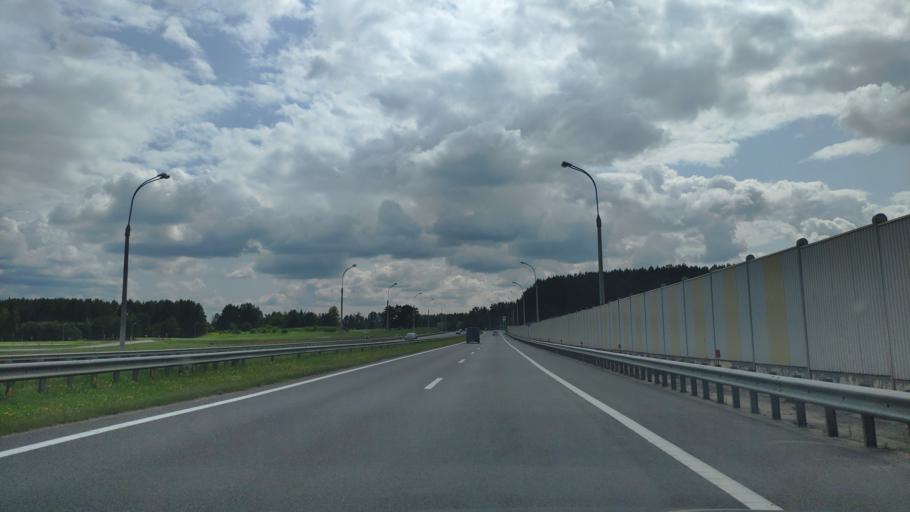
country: BY
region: Minsk
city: Zaslawye
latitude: 53.9969
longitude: 27.3064
